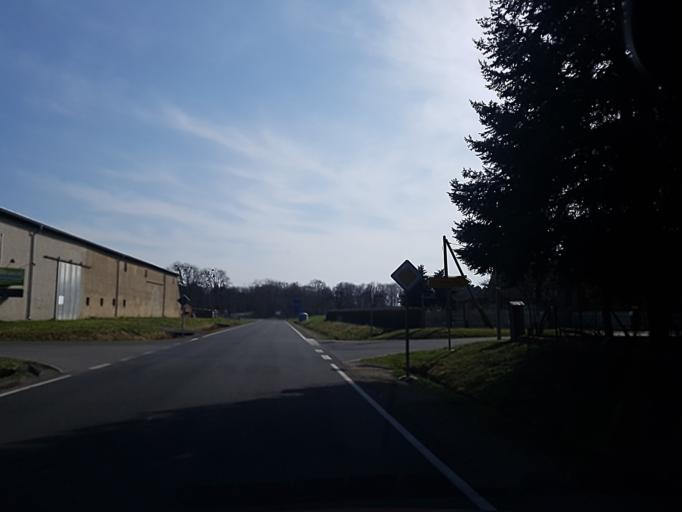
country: DE
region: Brandenburg
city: Bronkow
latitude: 51.6690
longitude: 13.9122
